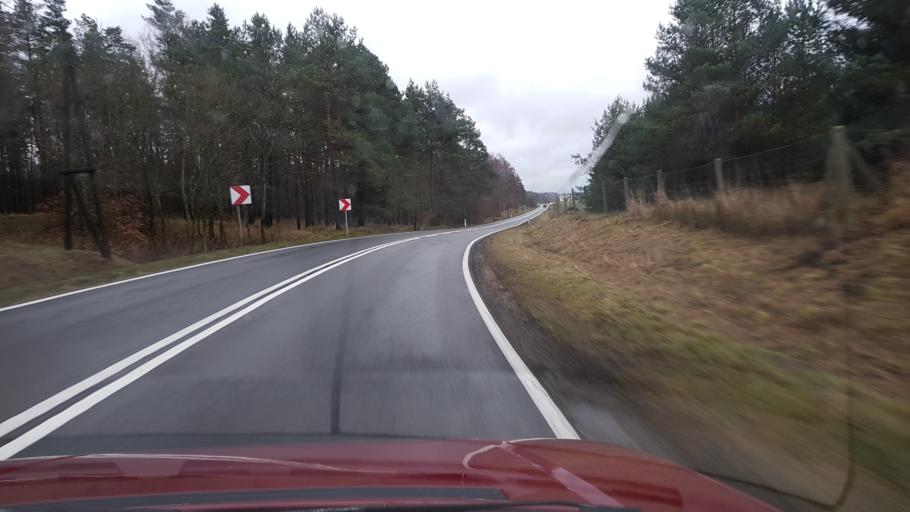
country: PL
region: West Pomeranian Voivodeship
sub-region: Powiat lobeski
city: Wegorzyno
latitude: 53.5191
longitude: 15.6343
